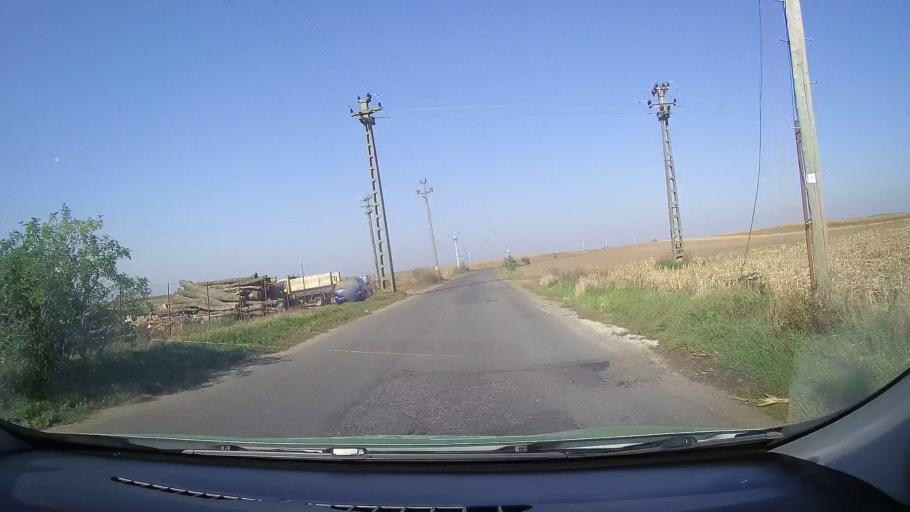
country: RO
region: Satu Mare
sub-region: Comuna Petresti
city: Petresti
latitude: 47.6098
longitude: 22.3552
